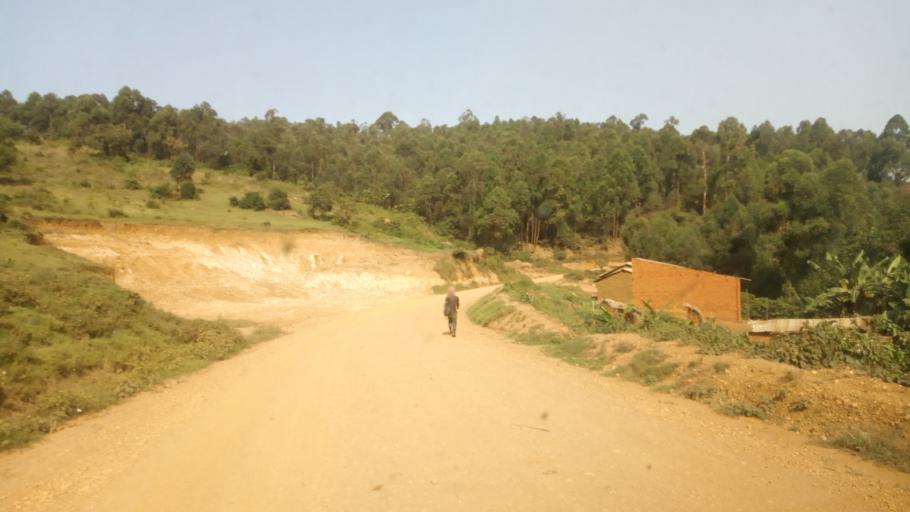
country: UG
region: Western Region
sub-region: Kanungu District
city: Ntungamo
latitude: -0.8314
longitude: 29.6962
